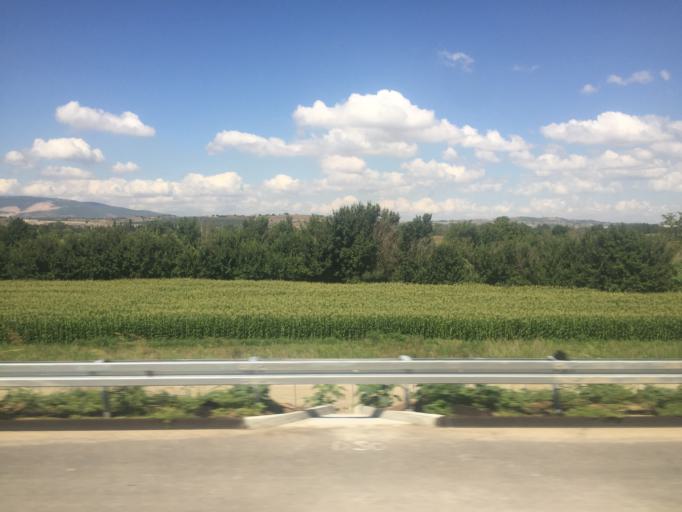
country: TR
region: Balikesir
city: Gobel
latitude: 39.9976
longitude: 28.1921
